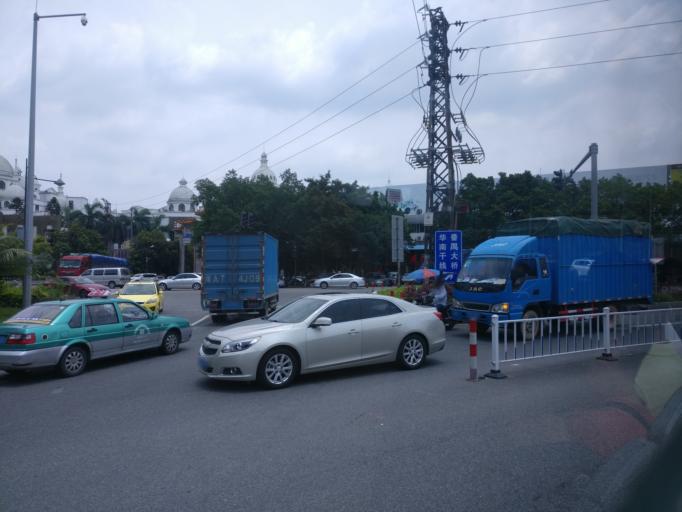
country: CN
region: Guangdong
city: Dashi
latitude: 23.0374
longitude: 113.3245
